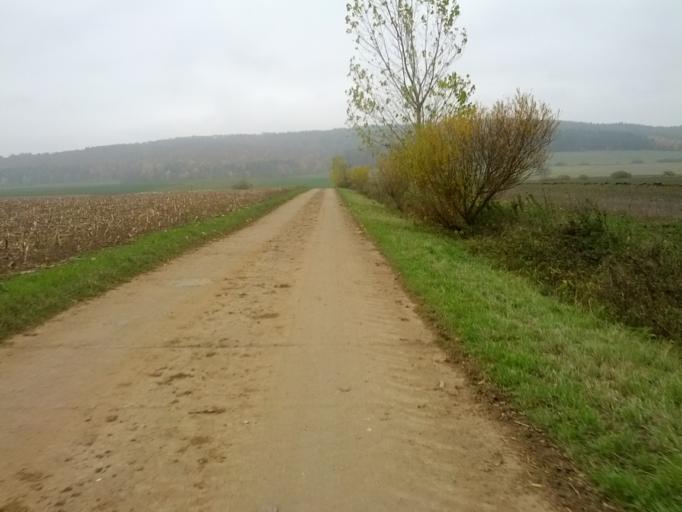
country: DE
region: Thuringia
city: Seebach
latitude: 50.9809
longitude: 10.4081
